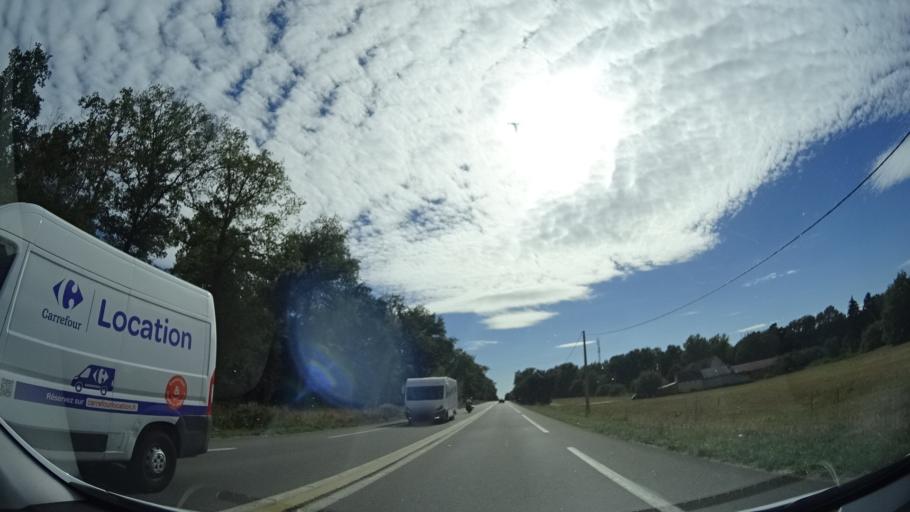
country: FR
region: Centre
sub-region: Departement du Loiret
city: Bellegarde
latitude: 47.9639
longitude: 2.3989
